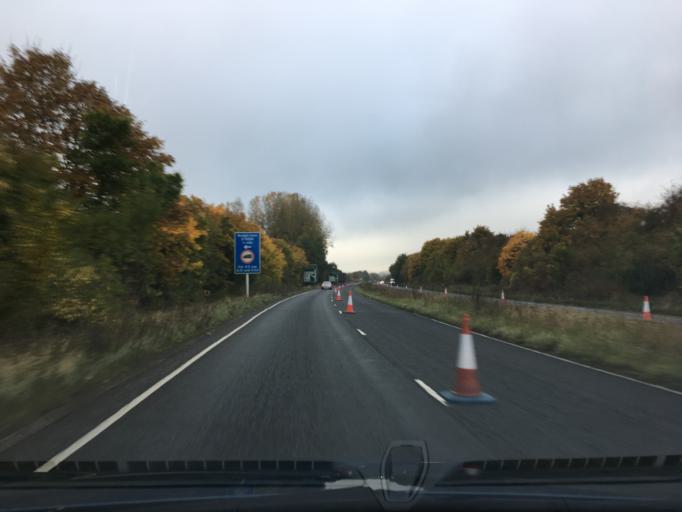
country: GB
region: England
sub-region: Hampshire
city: Alton
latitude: 51.1378
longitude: -0.9672
